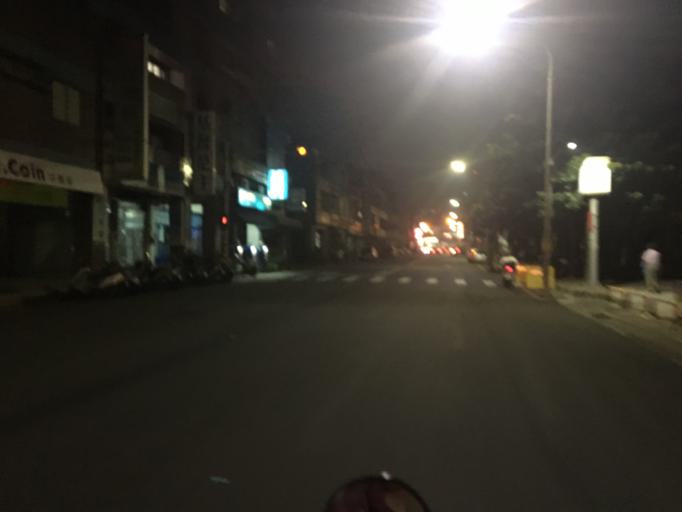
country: TW
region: Taiwan
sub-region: Hsinchu
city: Hsinchu
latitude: 24.8231
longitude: 120.9735
